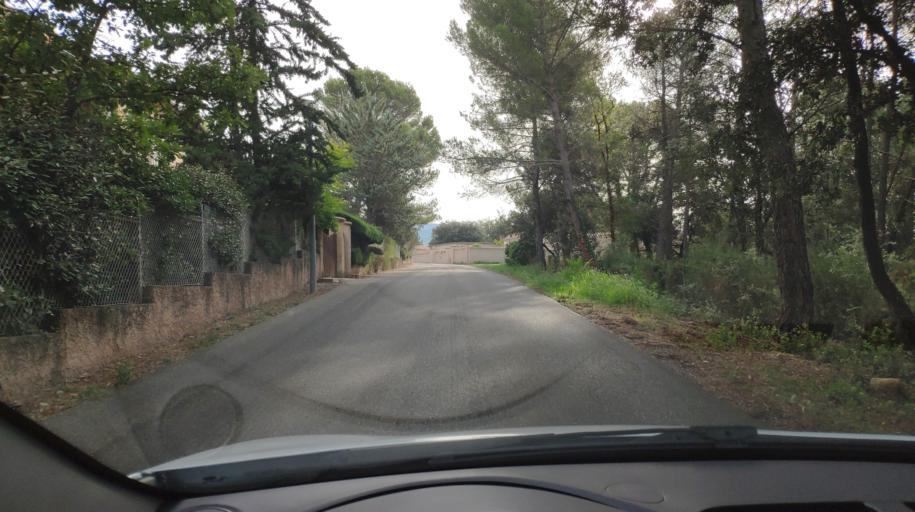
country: FR
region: Provence-Alpes-Cote d'Azur
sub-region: Departement du Vaucluse
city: Bedoin
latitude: 44.1171
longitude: 5.1877
